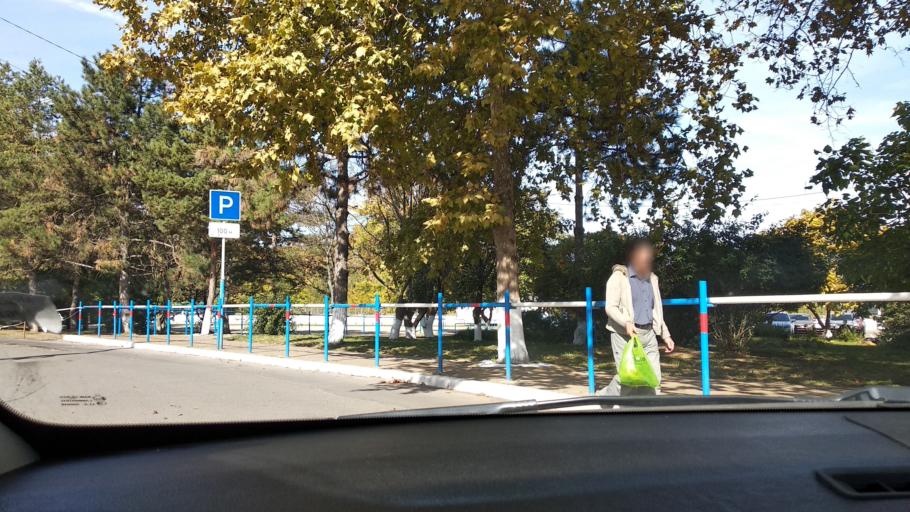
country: RU
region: Adygeya
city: Yablonovskiy
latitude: 45.0163
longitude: 38.9549
